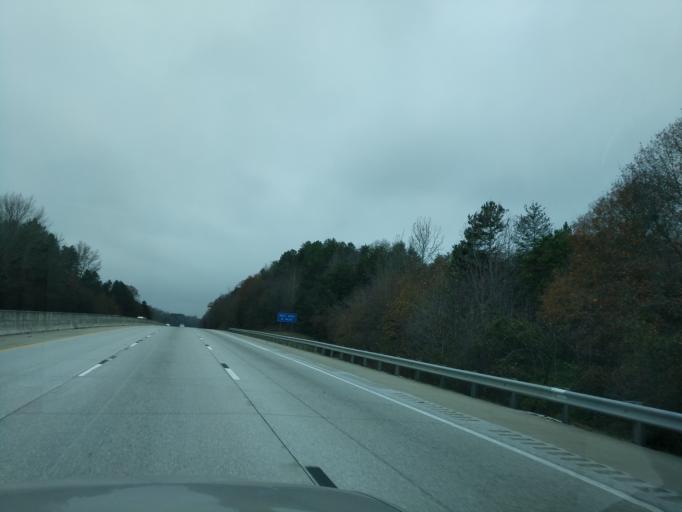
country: US
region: South Carolina
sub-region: Anderson County
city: Northlake
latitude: 34.6195
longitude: -82.6192
